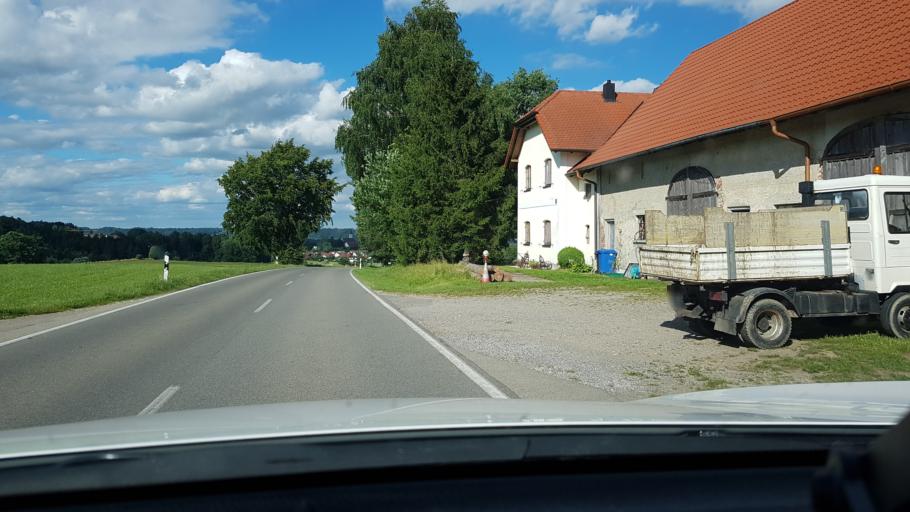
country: DE
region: Baden-Wuerttemberg
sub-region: Tuebingen Region
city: Kirchberg an der Iller
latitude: 48.1244
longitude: 10.0554
